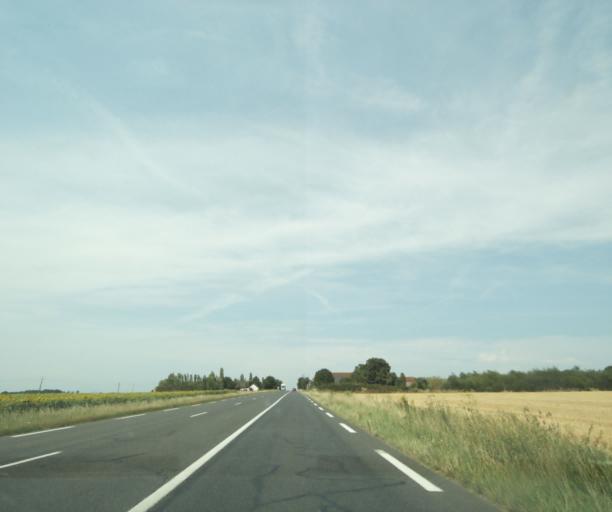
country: FR
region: Centre
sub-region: Departement d'Indre-et-Loire
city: Sainte-Maure-de-Touraine
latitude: 47.1702
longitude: 0.6534
